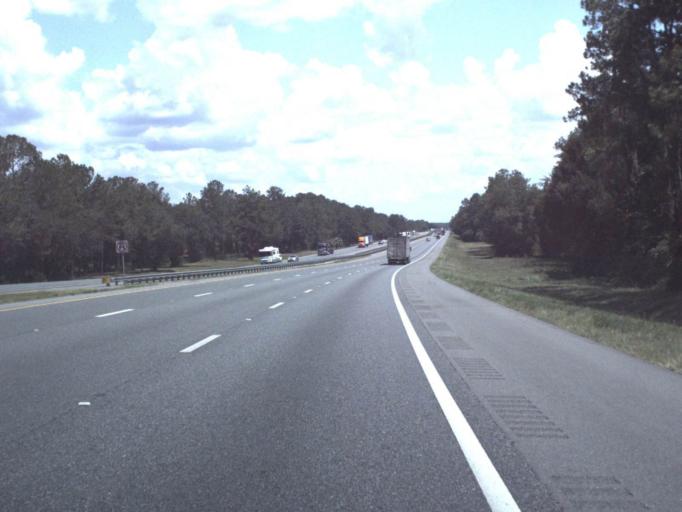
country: US
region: Florida
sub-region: Suwannee County
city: Wellborn
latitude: 30.3551
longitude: -82.8400
